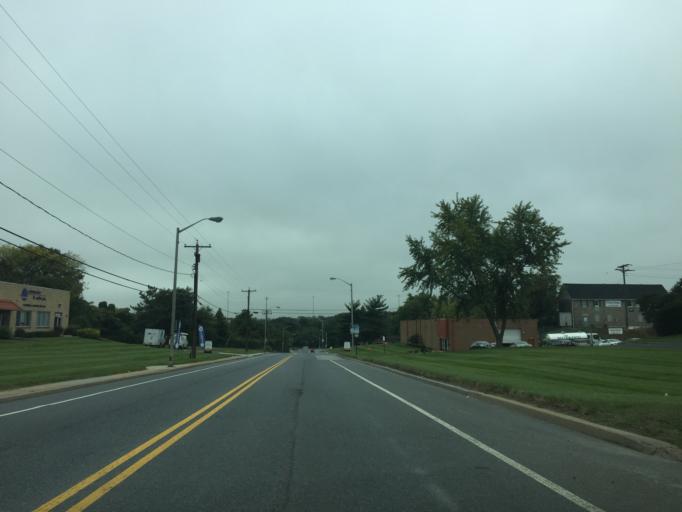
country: US
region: Maryland
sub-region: Baltimore County
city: Rosedale
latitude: 39.3110
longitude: -76.5351
